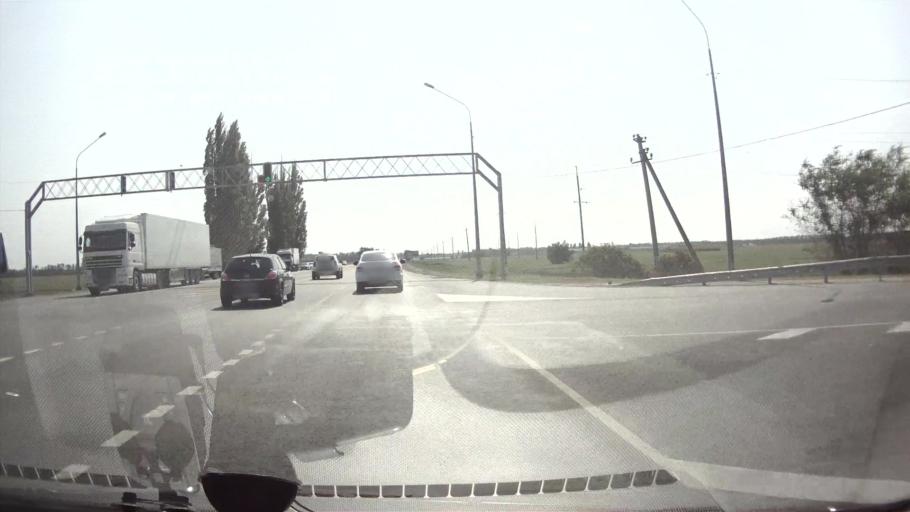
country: RU
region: Krasnodarskiy
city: Vasyurinskaya
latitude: 45.1121
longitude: 39.3887
